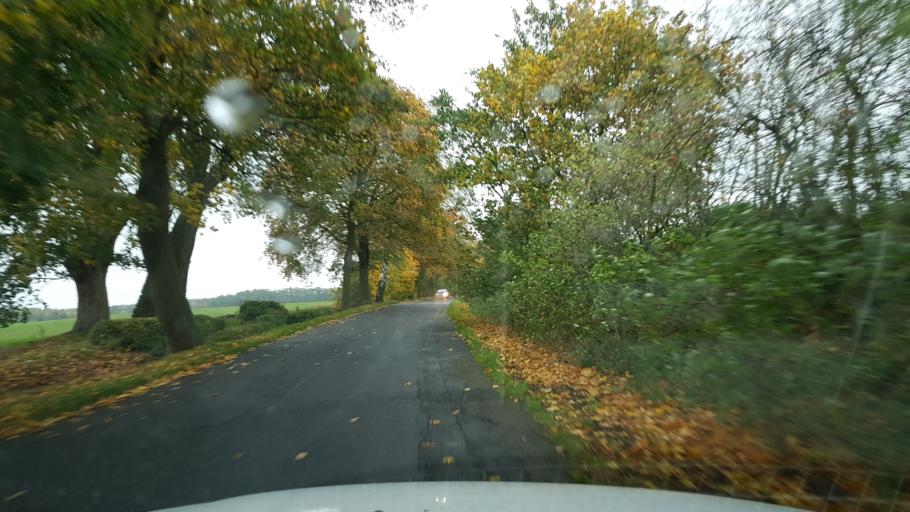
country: PL
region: West Pomeranian Voivodeship
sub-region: Powiat mysliborski
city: Mysliborz
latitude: 52.9777
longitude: 14.8759
